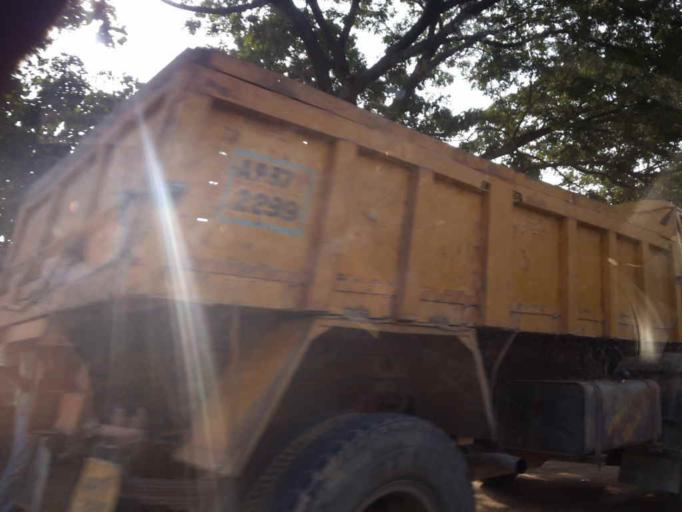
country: IN
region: Telangana
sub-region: Karimnagar
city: Kottapalli
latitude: 18.4368
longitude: 79.0232
